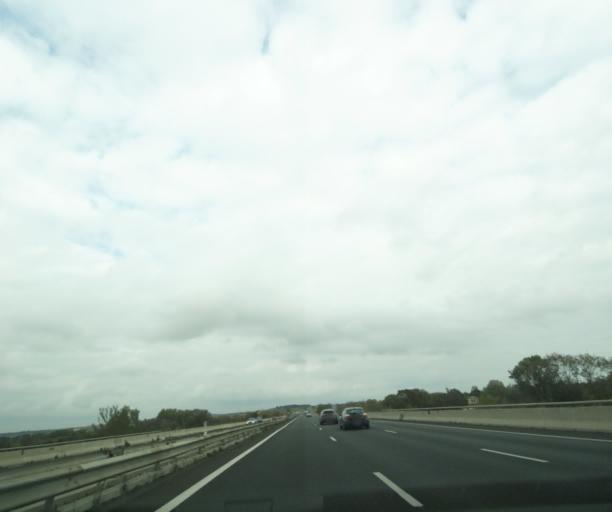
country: FR
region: Languedoc-Roussillon
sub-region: Departement de l'Herault
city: Florensac
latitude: 43.3850
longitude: 3.4535
